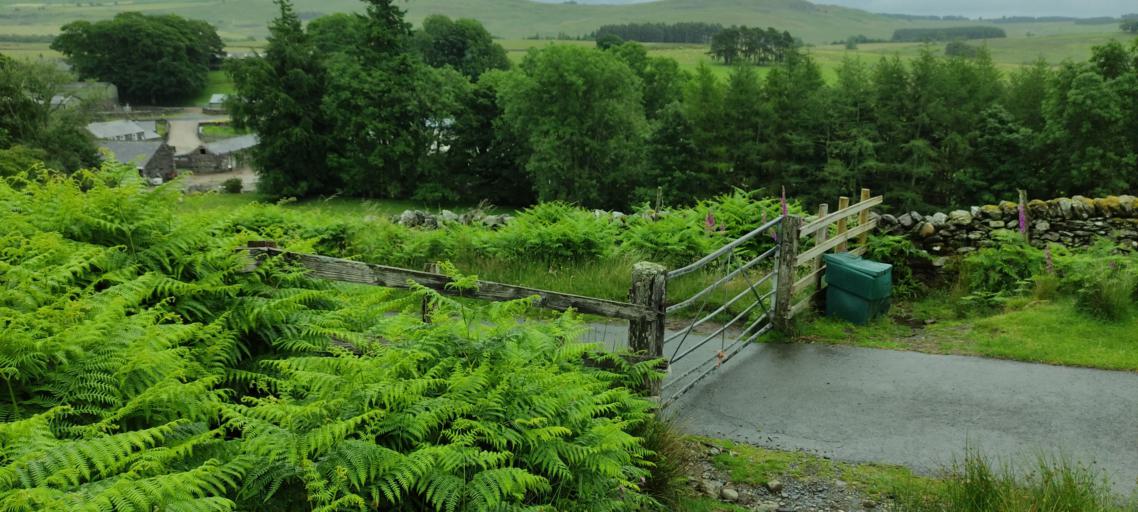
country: GB
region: England
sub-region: Cumbria
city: Keswick
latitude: 54.6585
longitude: -2.9874
